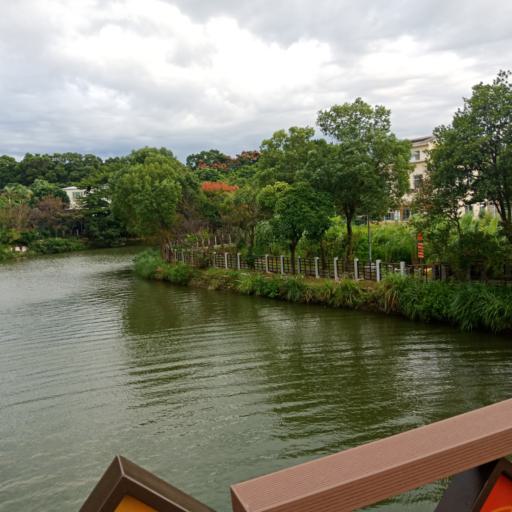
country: TW
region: Taiwan
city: Daxi
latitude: 24.8596
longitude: 121.2103
